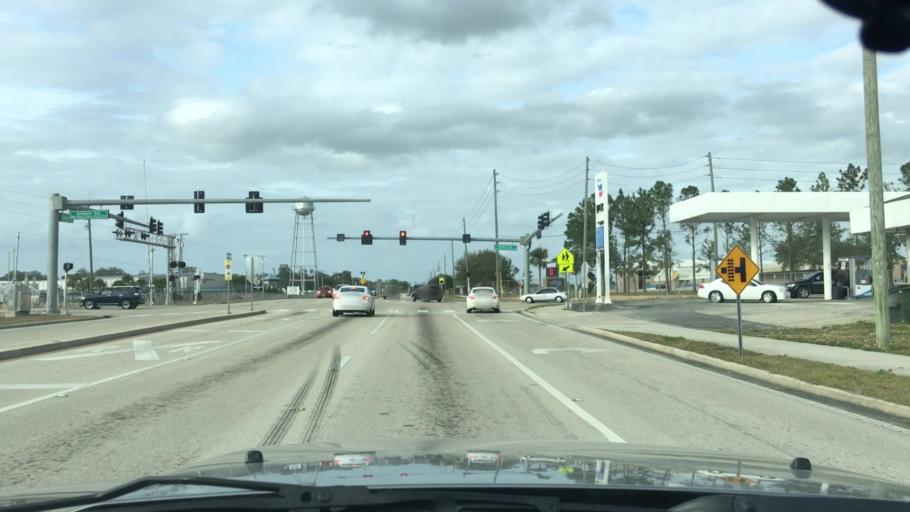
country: US
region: Florida
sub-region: Highlands County
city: Sebring
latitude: 27.4852
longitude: -81.4334
